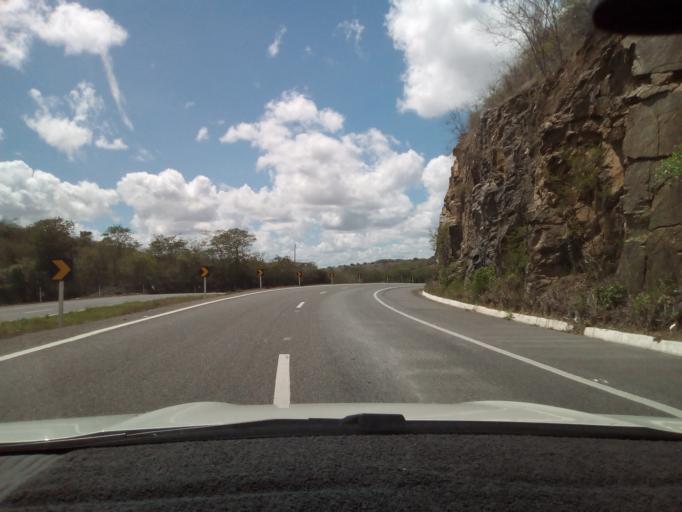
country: BR
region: Paraiba
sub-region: Fagundes
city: Fagundes
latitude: -7.2771
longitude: -35.7731
